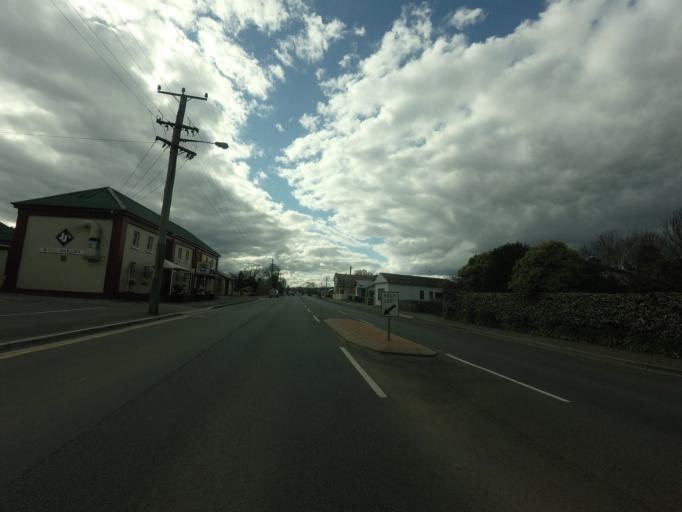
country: AU
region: Tasmania
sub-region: Northern Midlands
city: Longford
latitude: -41.5926
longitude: 147.1215
